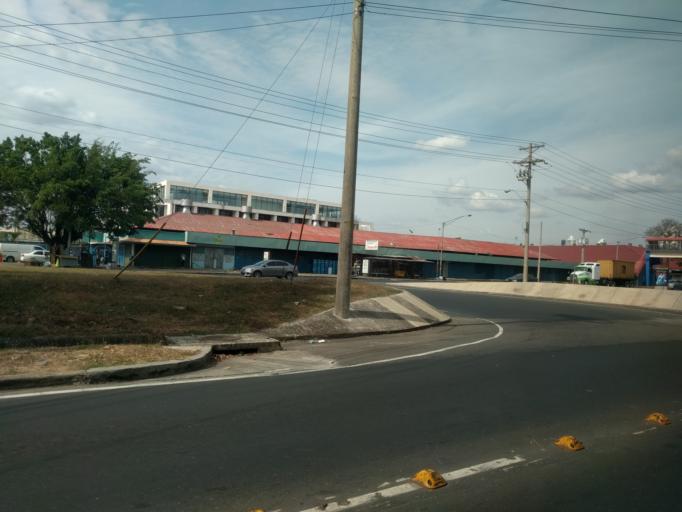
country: PA
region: Panama
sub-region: Distrito de Panama
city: Ancon
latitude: 8.9658
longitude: -79.5472
